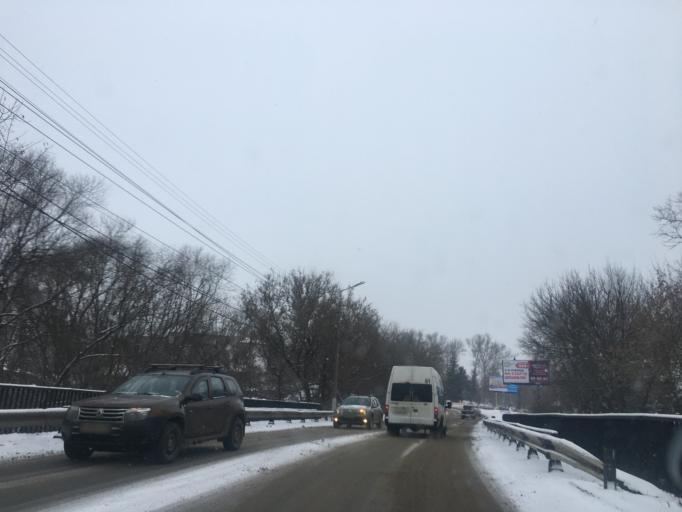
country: RU
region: Tula
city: Tula
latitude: 54.1928
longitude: 37.5665
